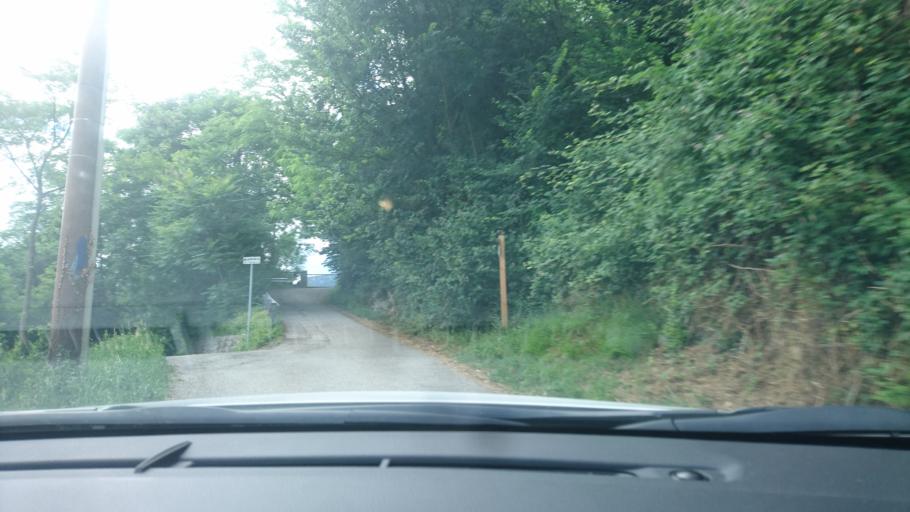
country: IT
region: Trentino-Alto Adige
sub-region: Provincia di Trento
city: Drena
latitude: 45.9691
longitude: 10.9621
